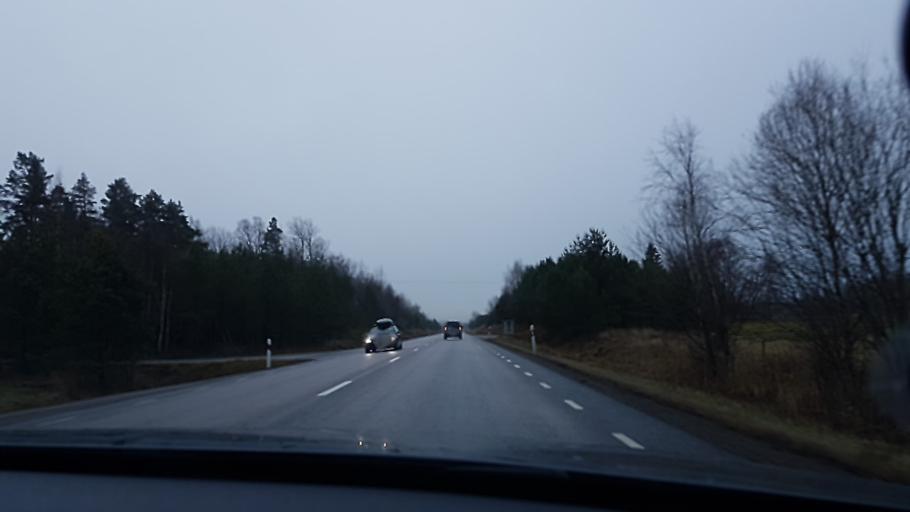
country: SE
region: Vaestra Goetaland
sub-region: Mariestads Kommun
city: Mariestad
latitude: 58.8050
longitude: 13.9749
